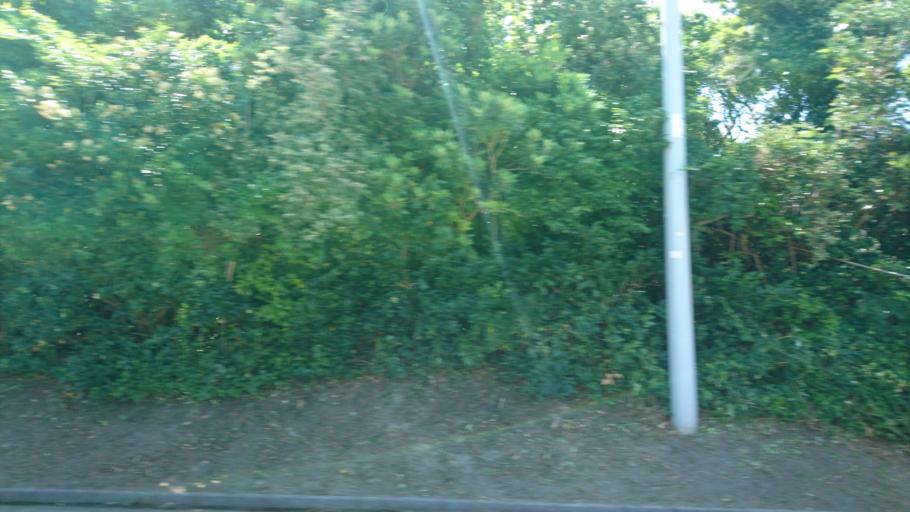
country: JP
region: Shizuoka
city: Shimoda
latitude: 34.3724
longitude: 139.2690
